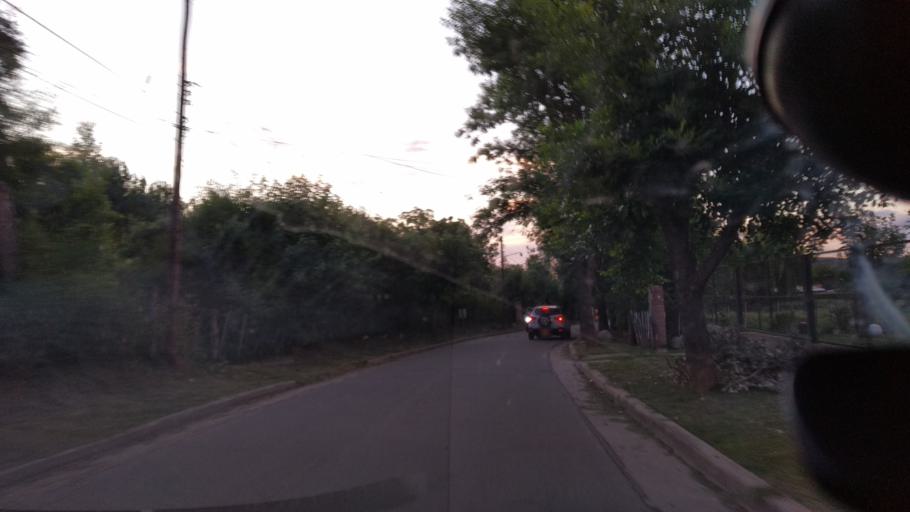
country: AR
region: Cordoba
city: Villa Las Rosas
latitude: -31.9456
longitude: -65.0604
